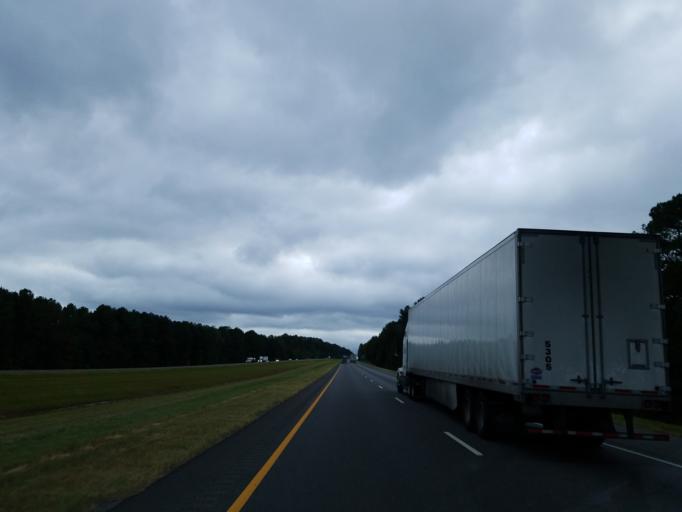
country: US
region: Alabama
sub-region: Hale County
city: Moundville
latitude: 32.9966
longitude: -87.7752
